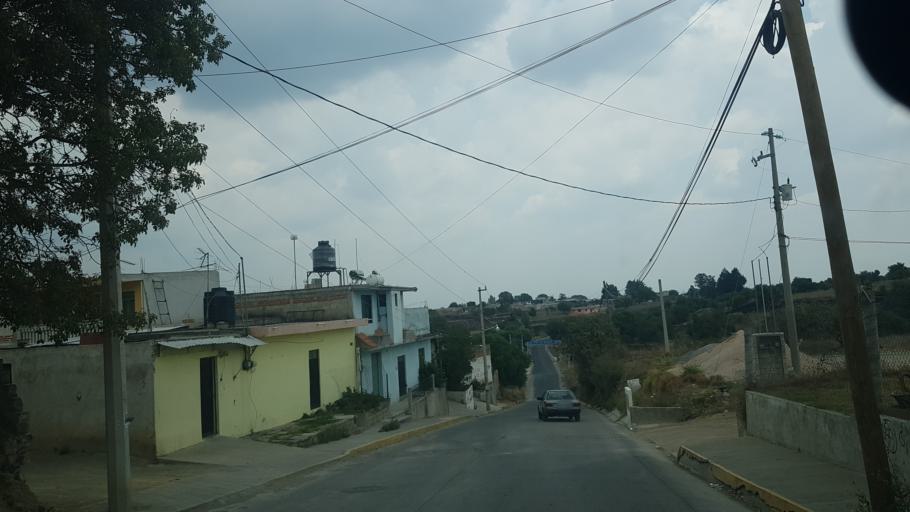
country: MX
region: Puebla
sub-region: Huejotzingo
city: San Miguel Tianguizolco
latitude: 19.1598
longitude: -98.4355
